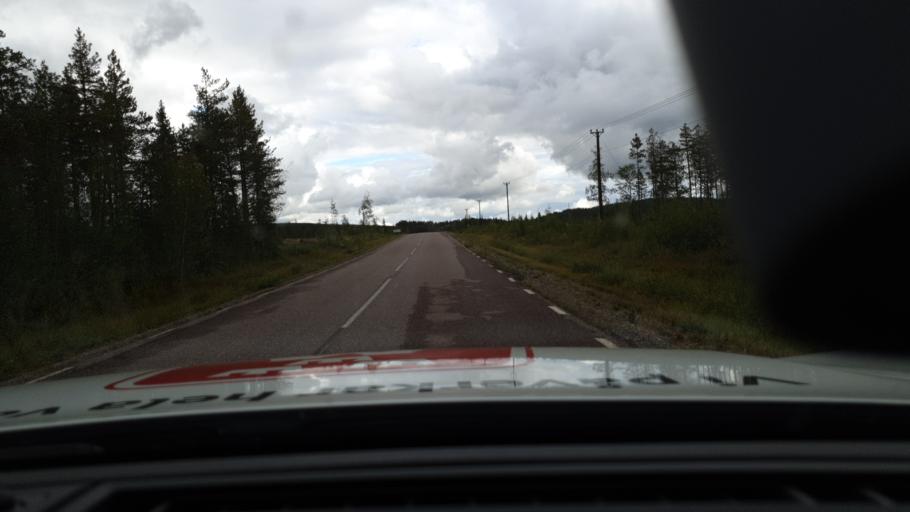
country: SE
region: Norrbotten
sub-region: Gallivare Kommun
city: Gaellivare
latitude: 66.9183
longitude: 21.6816
